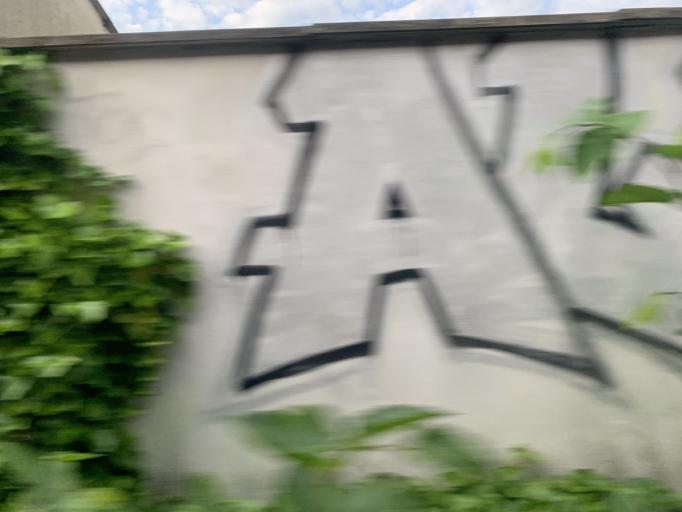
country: FR
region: Rhone-Alpes
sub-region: Departement du Rhone
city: Meyzieu
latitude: 45.7701
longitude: 5.0113
